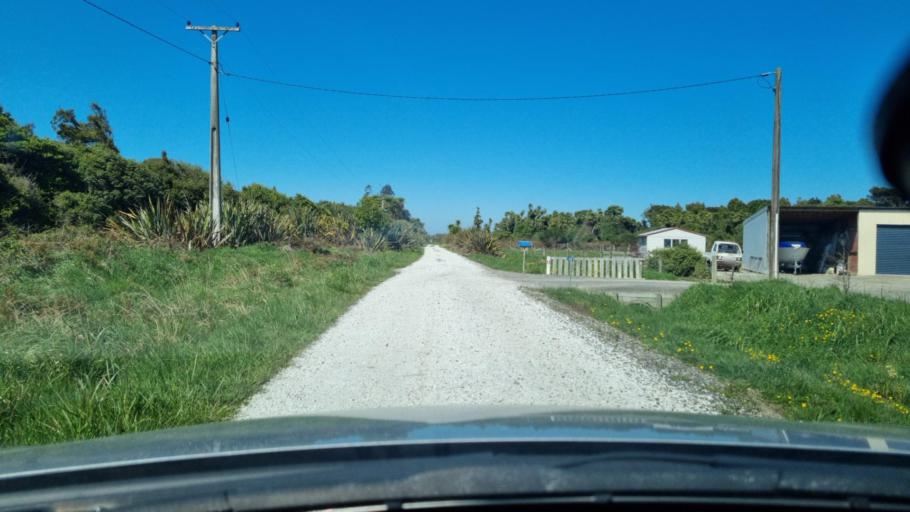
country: NZ
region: Southland
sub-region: Invercargill City
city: Invercargill
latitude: -46.4519
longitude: 168.3166
